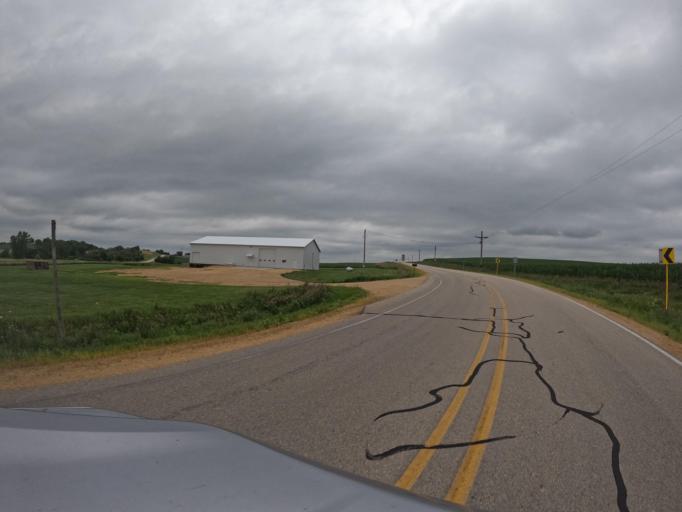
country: US
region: Iowa
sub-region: Clinton County
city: De Witt
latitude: 41.9311
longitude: -90.6068
